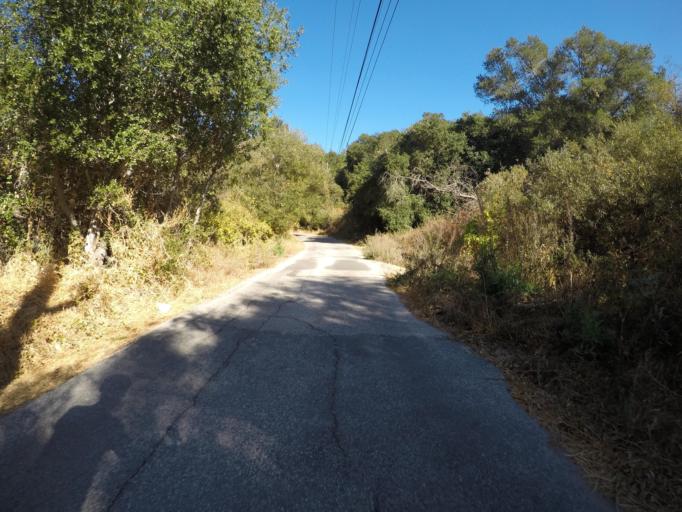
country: US
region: California
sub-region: Santa Cruz County
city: Scotts Valley
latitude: 37.0799
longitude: -121.9981
